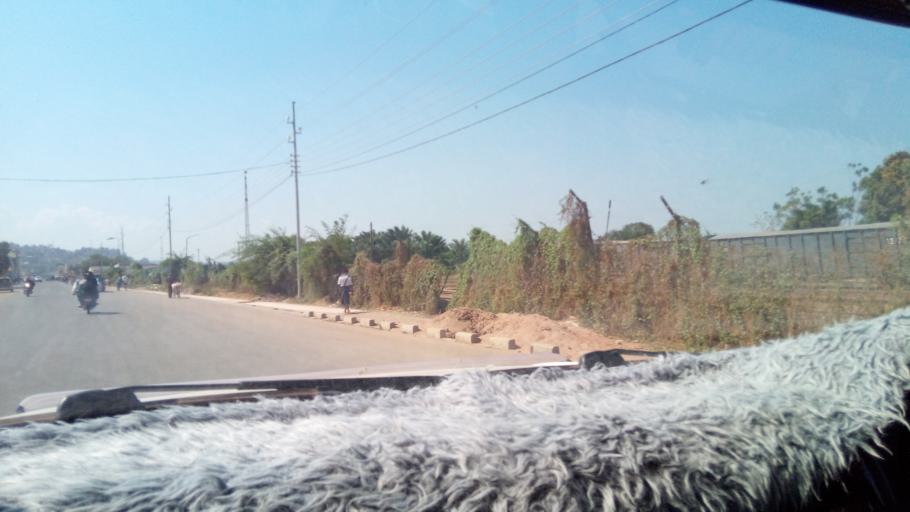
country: CD
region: Katanga
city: Kalemie
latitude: -5.9449
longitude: 29.1976
